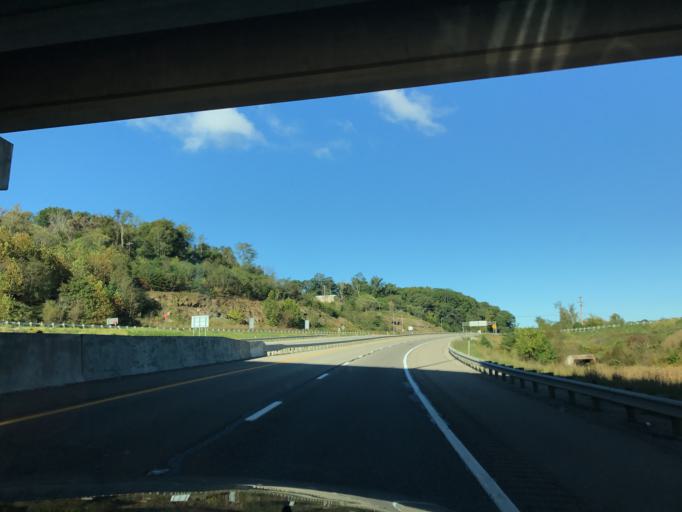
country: US
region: West Virginia
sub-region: Wood County
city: Blennerhassett
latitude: 39.2519
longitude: -81.6116
